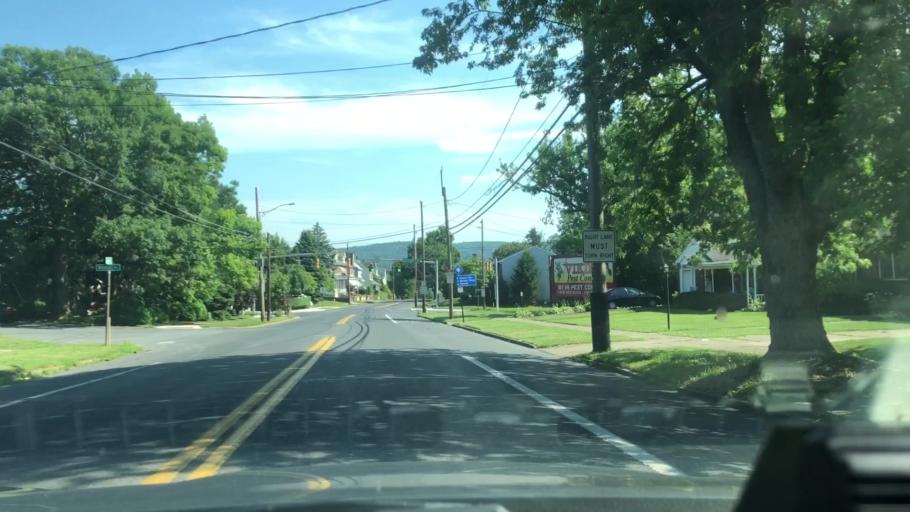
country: US
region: Pennsylvania
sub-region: Northampton County
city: Bethlehem
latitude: 40.6360
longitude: -75.3752
